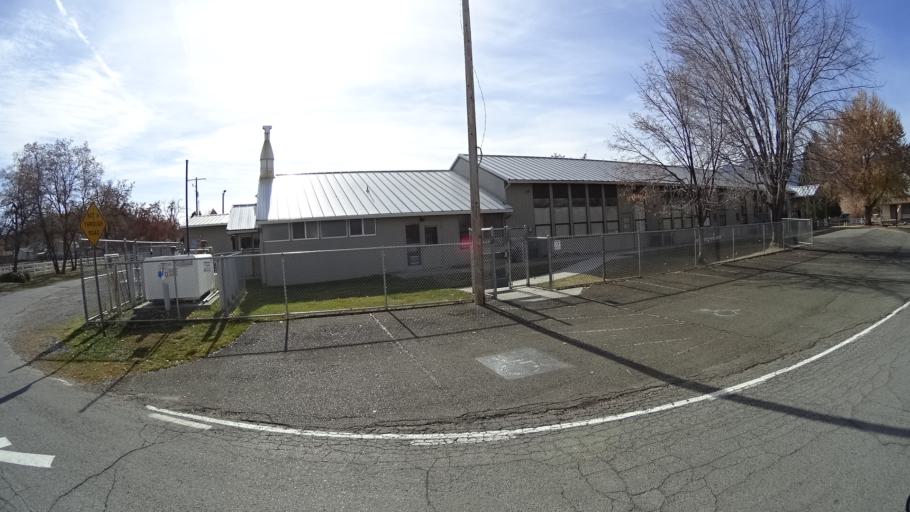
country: US
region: California
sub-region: Siskiyou County
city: Weed
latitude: 41.4578
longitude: -122.4312
